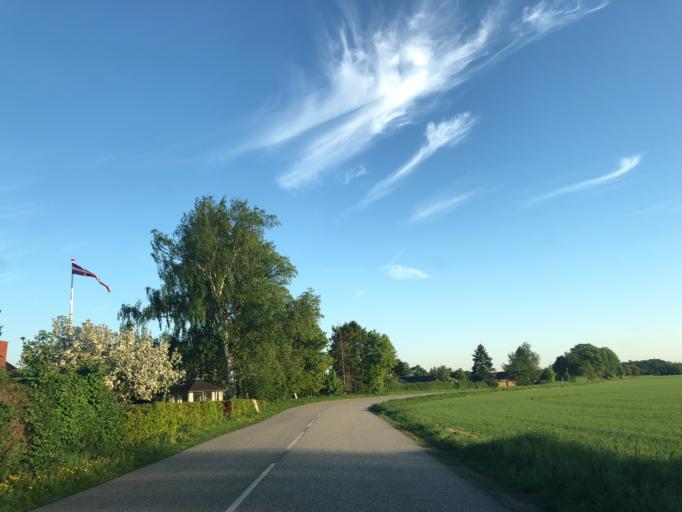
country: DK
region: Zealand
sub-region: Koge Kommune
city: Borup
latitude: 55.4465
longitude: 11.9520
